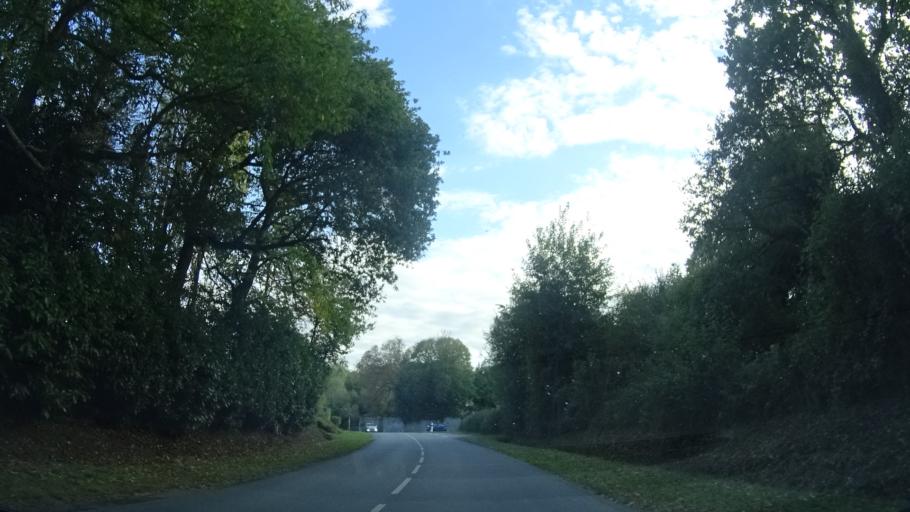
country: FR
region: Brittany
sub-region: Departement d'Ille-et-Vilaine
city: Le Minihic-sur-Rance
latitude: 48.5661
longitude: -2.0137
